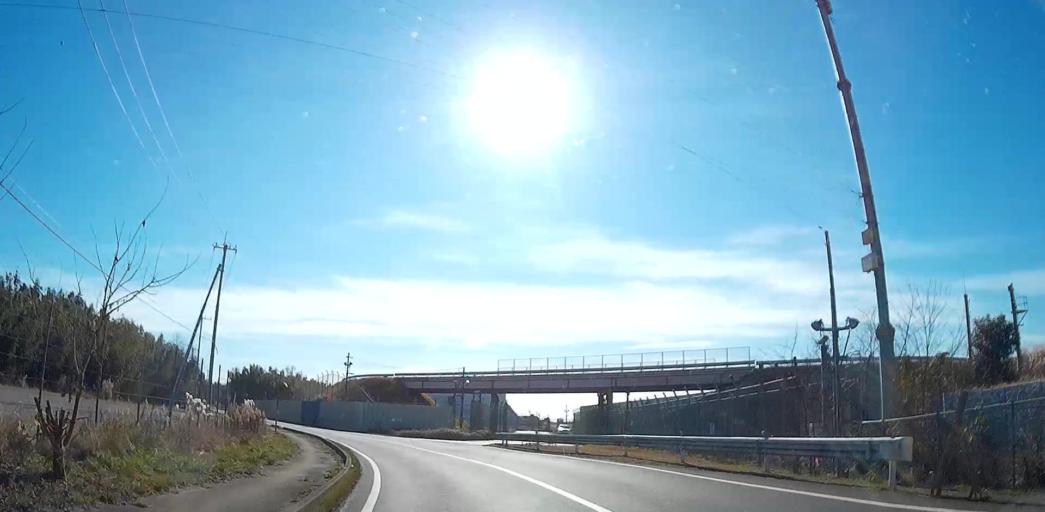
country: JP
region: Chiba
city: Narita
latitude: 35.7883
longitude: 140.3962
